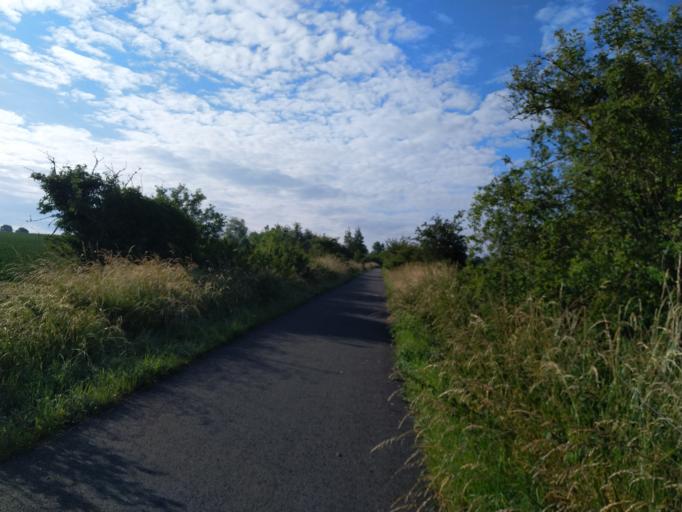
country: BE
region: Wallonia
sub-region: Province du Hainaut
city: Binche
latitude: 50.4299
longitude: 4.1564
